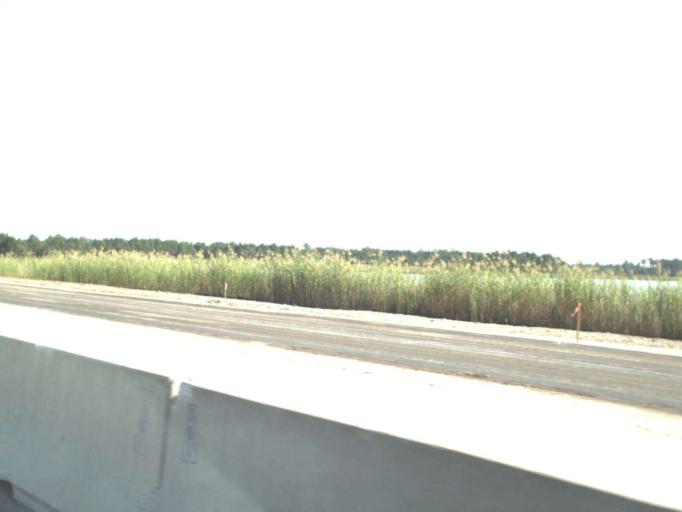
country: US
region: Florida
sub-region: Walton County
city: Freeport
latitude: 30.4283
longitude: -86.1555
